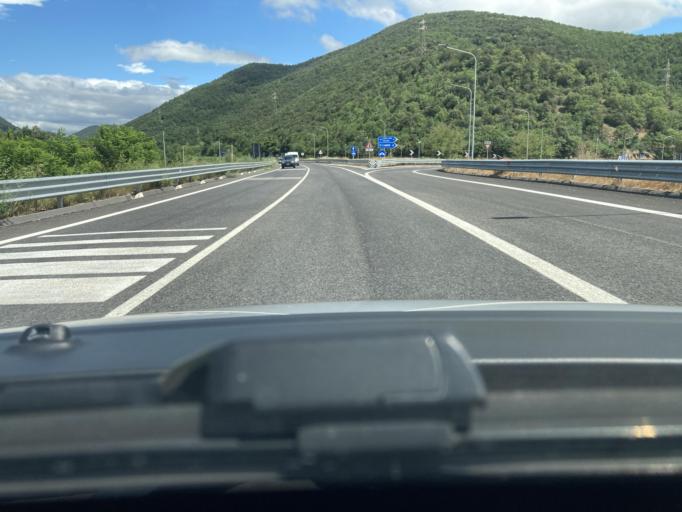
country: IT
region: Latium
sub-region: Provincia di Rieti
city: Colli sul Velino
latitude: 42.5083
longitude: 12.7470
